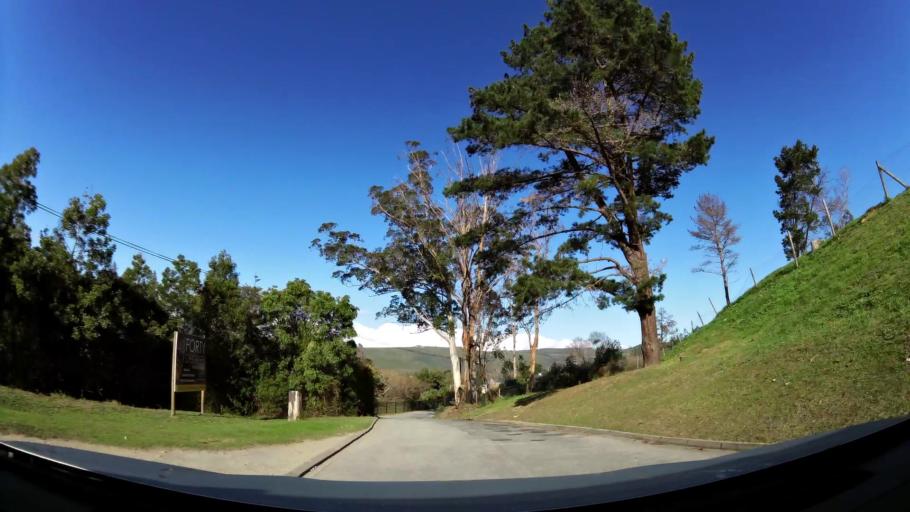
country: ZA
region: Western Cape
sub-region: Eden District Municipality
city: Knysna
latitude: -34.0339
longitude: 23.0197
